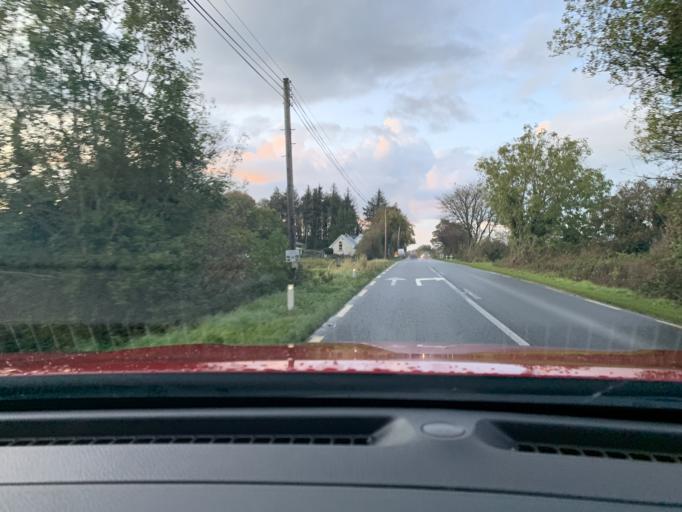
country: IE
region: Connaught
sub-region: Sligo
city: Ballymote
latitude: 54.0873
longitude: -8.3853
